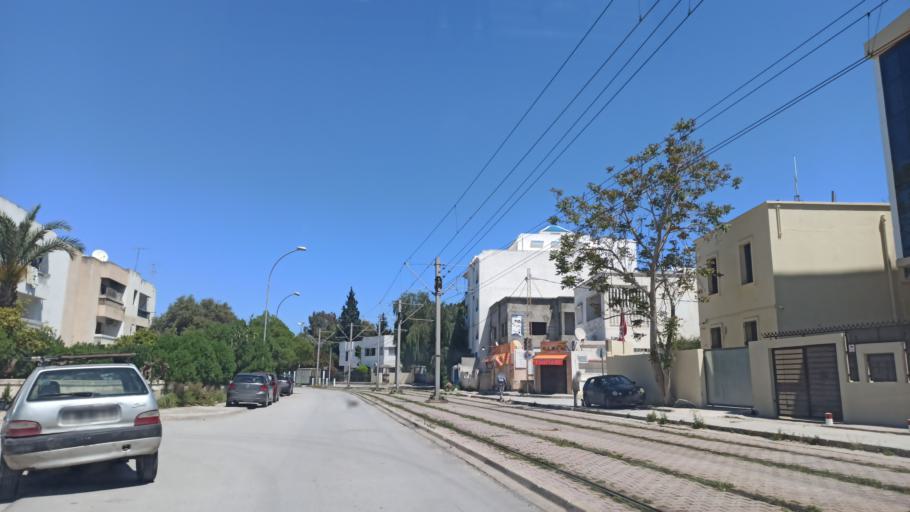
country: TN
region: Tunis
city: Tunis
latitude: 36.8224
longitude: 10.1847
